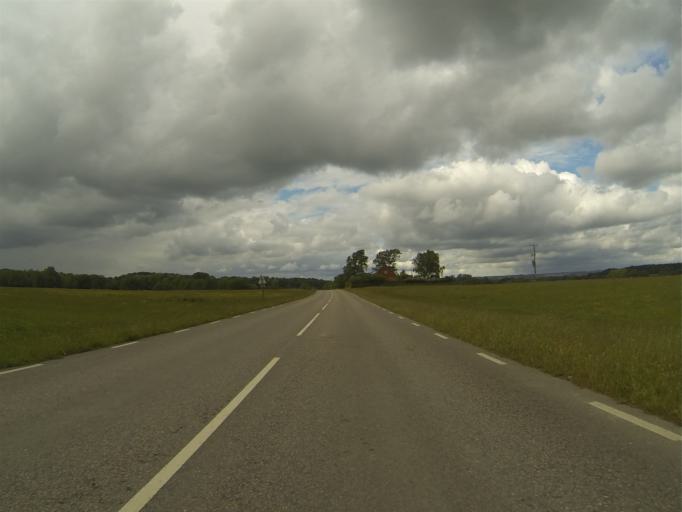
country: SE
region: Skane
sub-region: Lunds Kommun
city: Veberod
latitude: 55.6857
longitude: 13.4245
